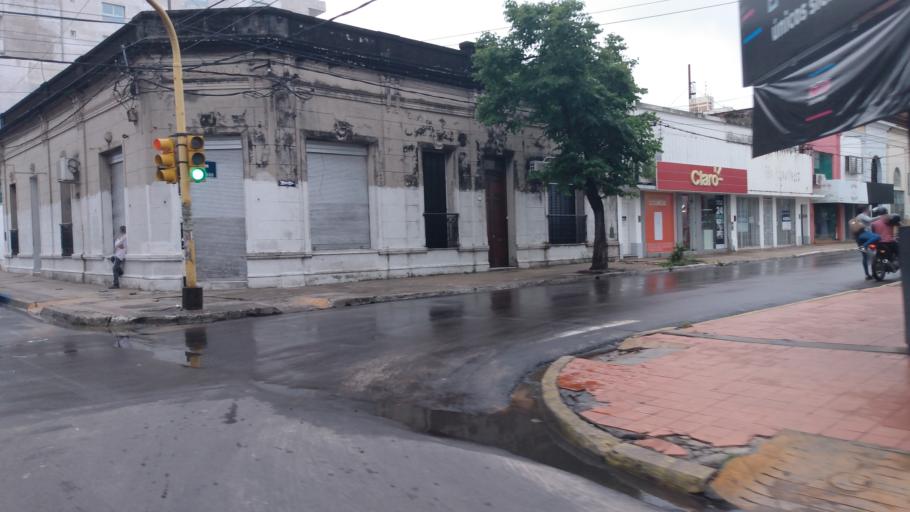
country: AR
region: Corrientes
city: Corrientes
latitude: -27.4691
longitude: -58.8332
